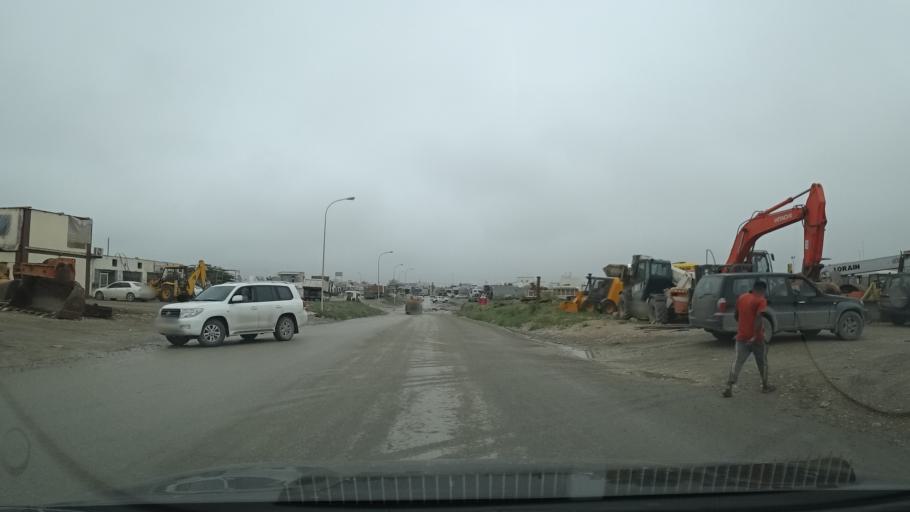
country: OM
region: Zufar
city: Salalah
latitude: 17.0287
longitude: 54.0440
